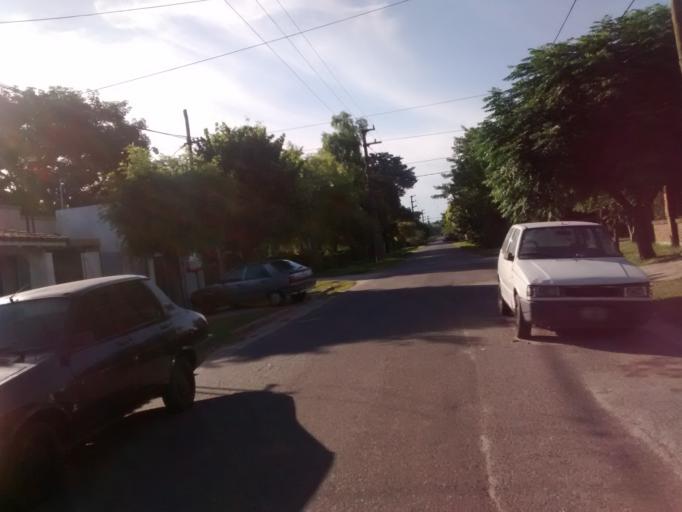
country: AR
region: Buenos Aires
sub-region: Partido de La Plata
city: La Plata
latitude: -34.8583
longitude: -58.0765
